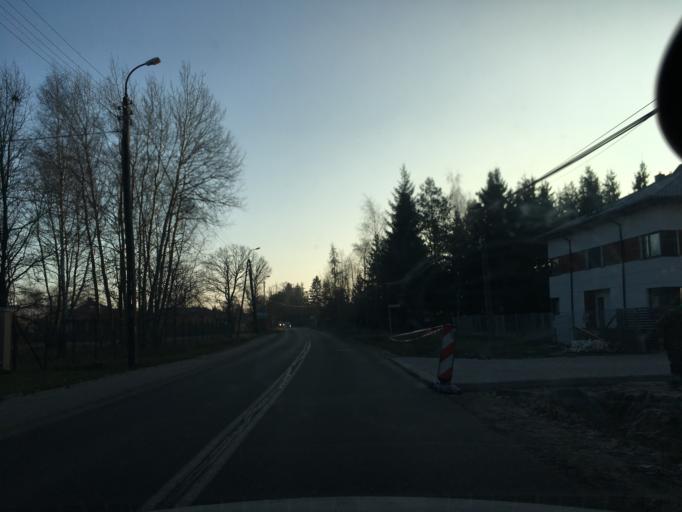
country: PL
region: Masovian Voivodeship
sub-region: Powiat piaseczynski
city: Piaseczno
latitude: 52.0700
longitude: 20.9834
